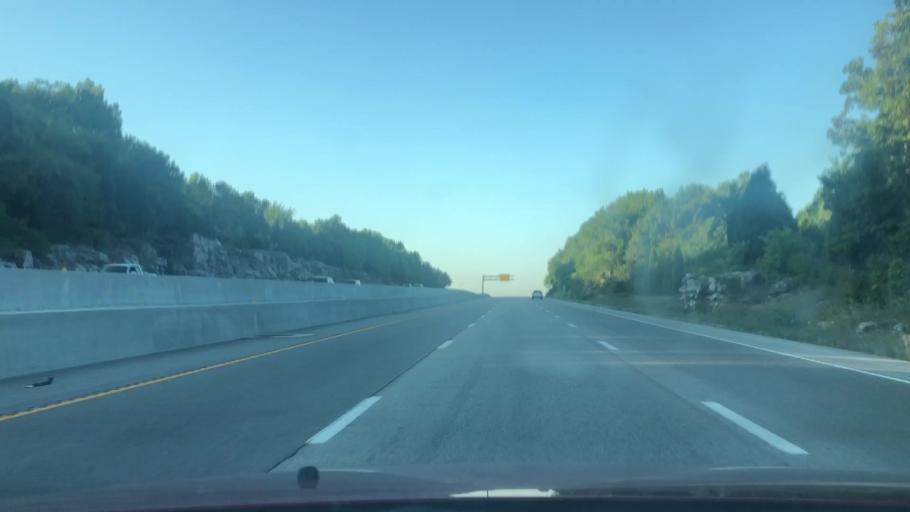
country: US
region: Missouri
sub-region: Christian County
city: Nixa
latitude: 37.1097
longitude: -93.2336
